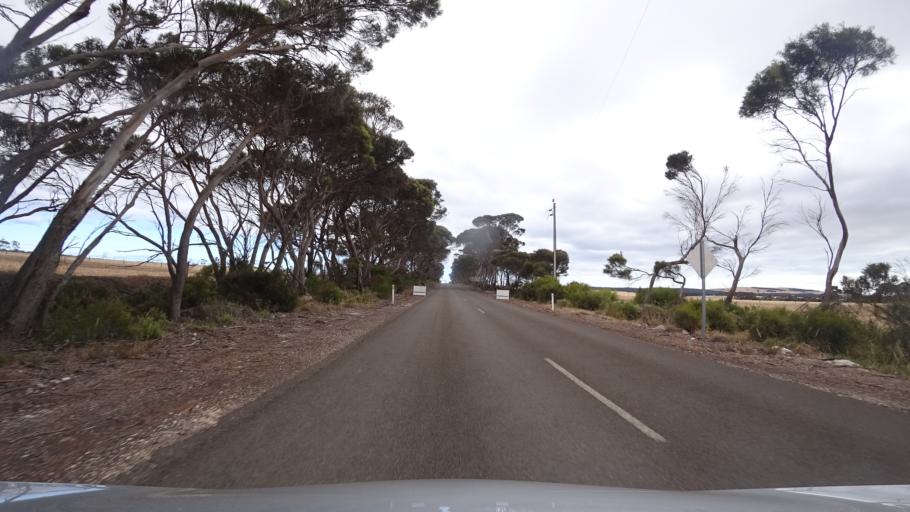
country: AU
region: South Australia
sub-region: Kangaroo Island
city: Kingscote
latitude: -35.6234
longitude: 137.5305
